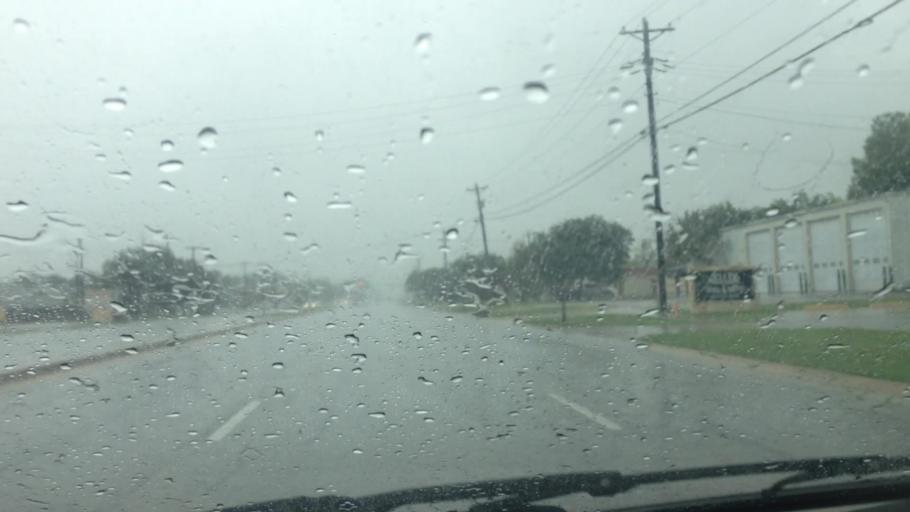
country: US
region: Texas
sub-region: Tarrant County
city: Keller
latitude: 32.9344
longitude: -97.2400
